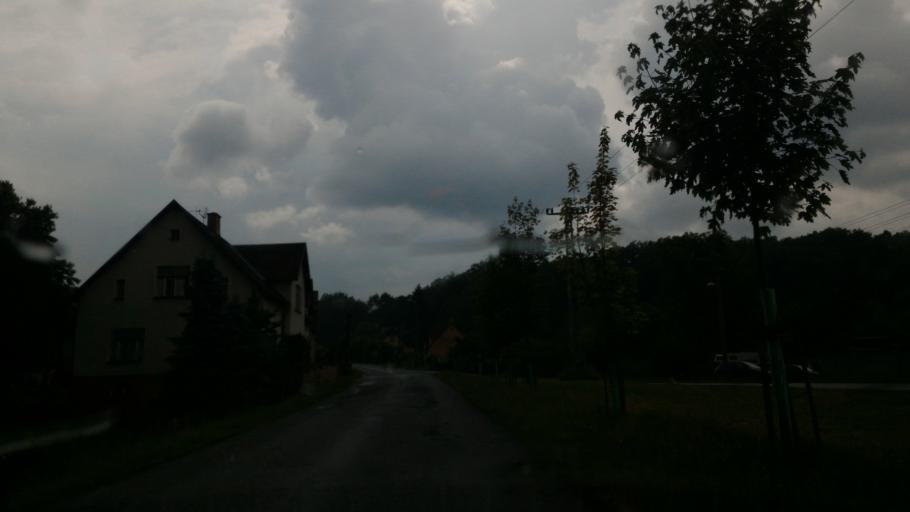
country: CZ
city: Hradek nad Nisou
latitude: 50.8441
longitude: 14.8461
